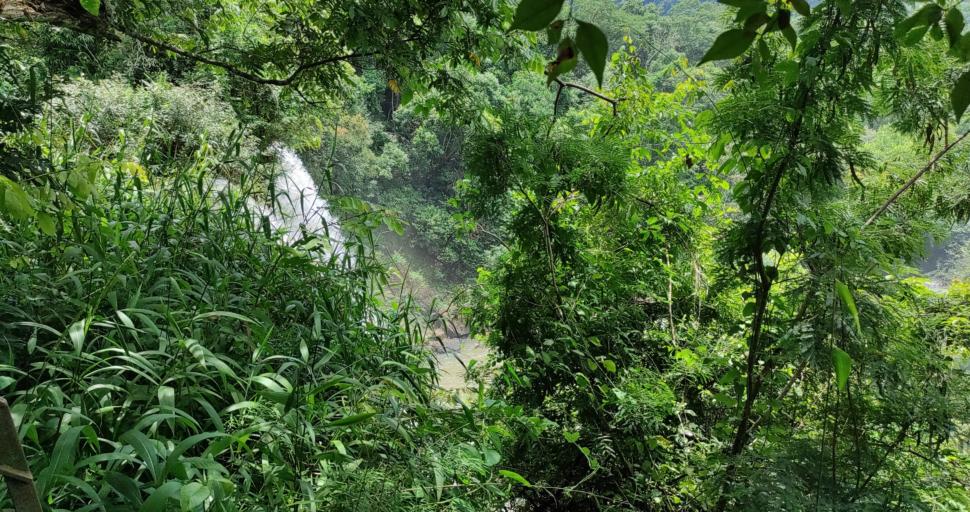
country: AR
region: Misiones
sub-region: Departamento de Iguazu
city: Puerto Iguazu
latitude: -25.6842
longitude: -54.4458
